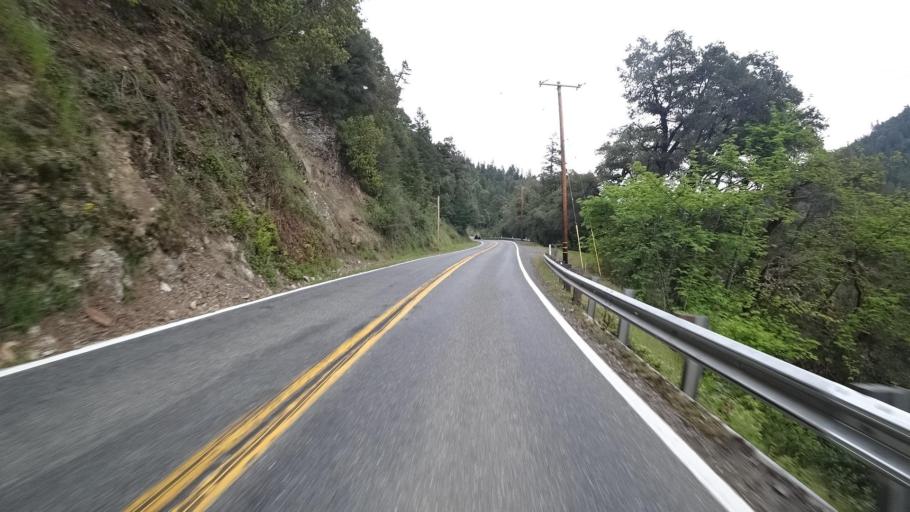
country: US
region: California
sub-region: Humboldt County
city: Willow Creek
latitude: 40.9910
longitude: -123.6367
